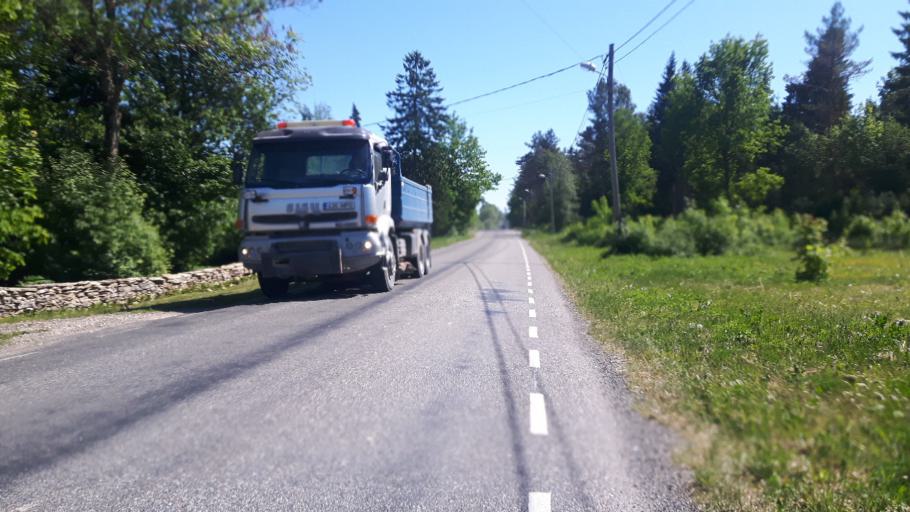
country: EE
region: Raplamaa
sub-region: Kohila vald
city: Kohila
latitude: 59.1746
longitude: 24.7328
